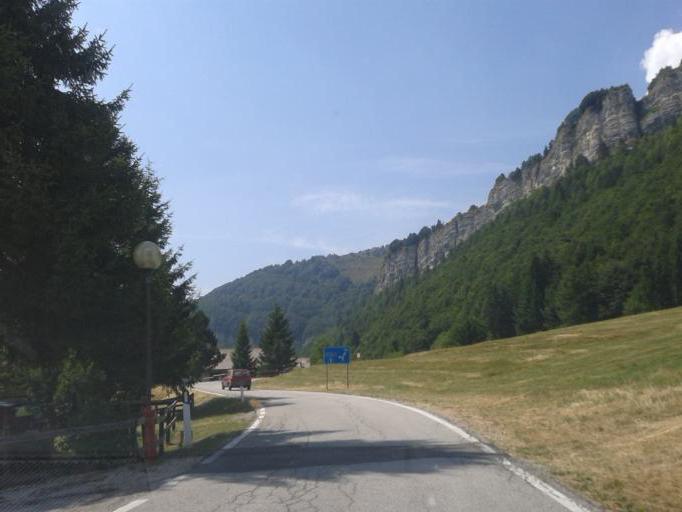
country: IT
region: Trentino-Alto Adige
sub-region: Provincia di Trento
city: Avio
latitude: 45.7823
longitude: 10.9080
